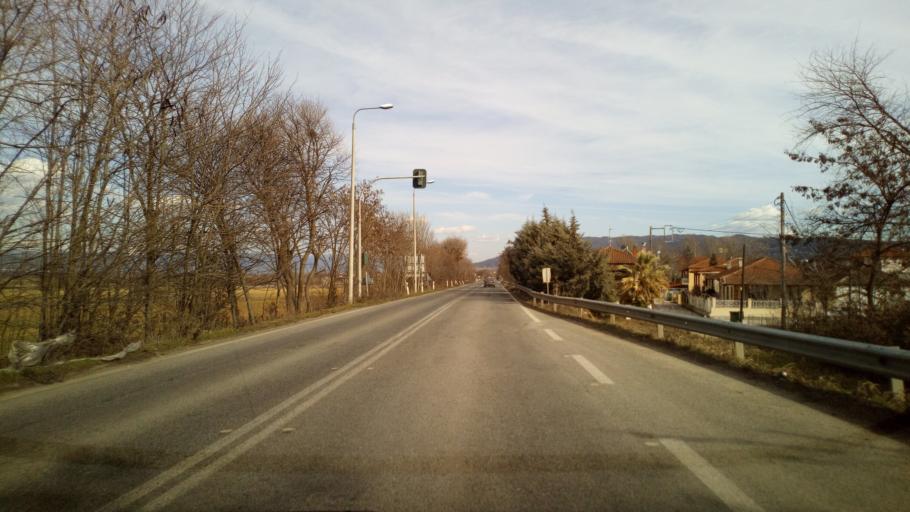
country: GR
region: Central Macedonia
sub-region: Nomos Thessalonikis
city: Gerakarou
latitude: 40.6311
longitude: 23.2178
